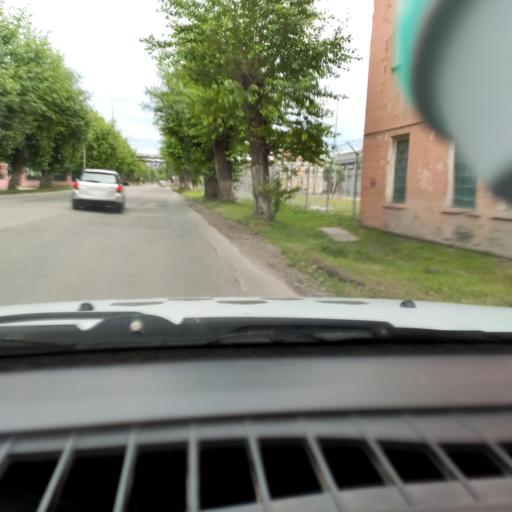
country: RU
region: Perm
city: Chusovoy
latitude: 58.2942
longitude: 57.8143
